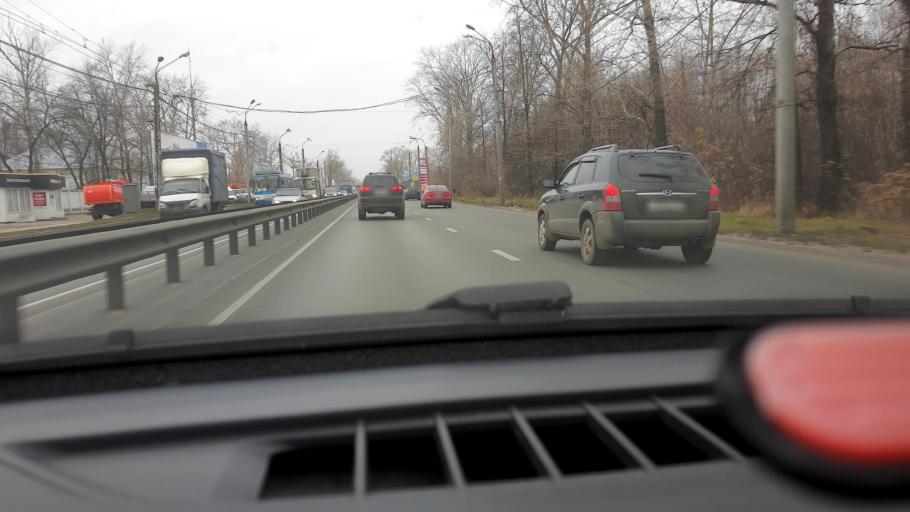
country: RU
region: Nizjnij Novgorod
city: Gorbatovka
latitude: 56.3133
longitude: 43.8449
